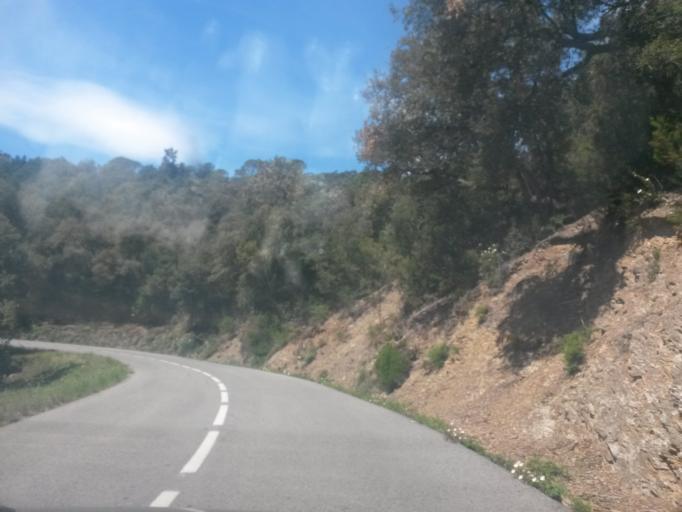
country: ES
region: Catalonia
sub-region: Provincia de Girona
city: Cassa de la Selva
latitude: 41.9304
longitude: 2.9195
